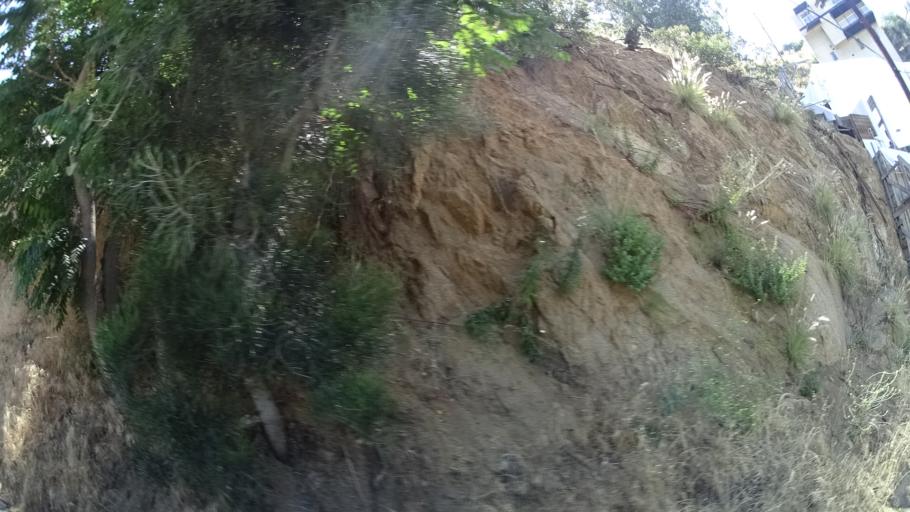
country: US
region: California
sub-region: Los Angeles County
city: West Hollywood
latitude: 34.0982
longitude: -118.3781
